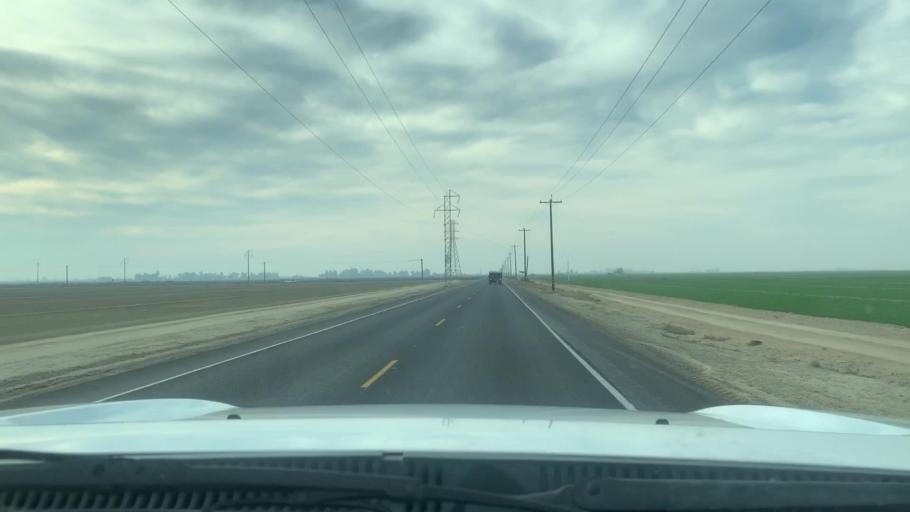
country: US
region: California
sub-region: Kern County
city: Buttonwillow
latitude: 35.4421
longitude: -119.3728
